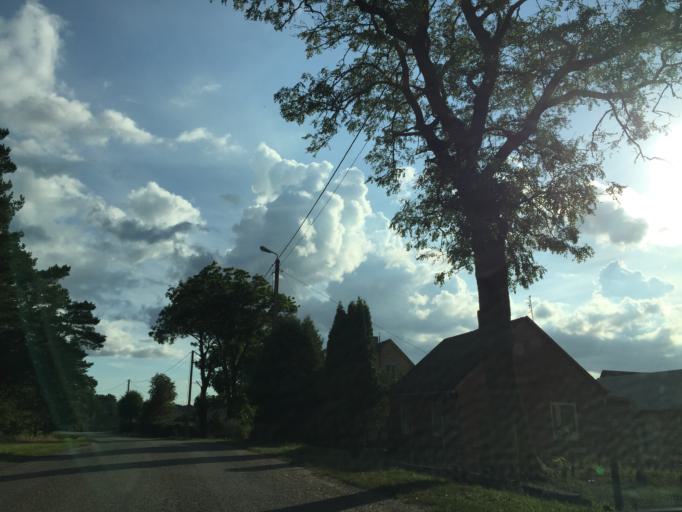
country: LT
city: Zagare
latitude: 56.3707
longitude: 23.2677
